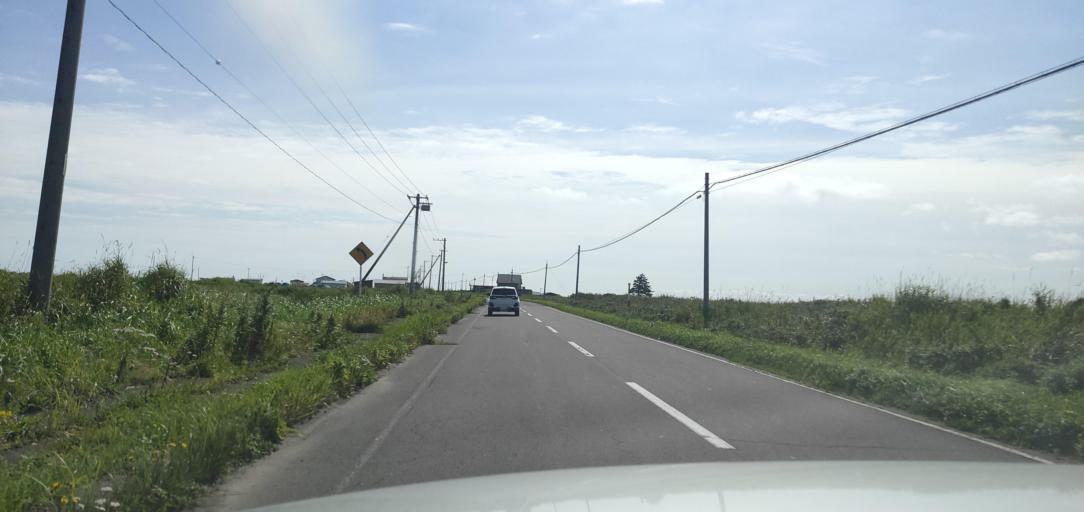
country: JP
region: Hokkaido
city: Shibetsu
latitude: 43.6302
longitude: 145.1904
